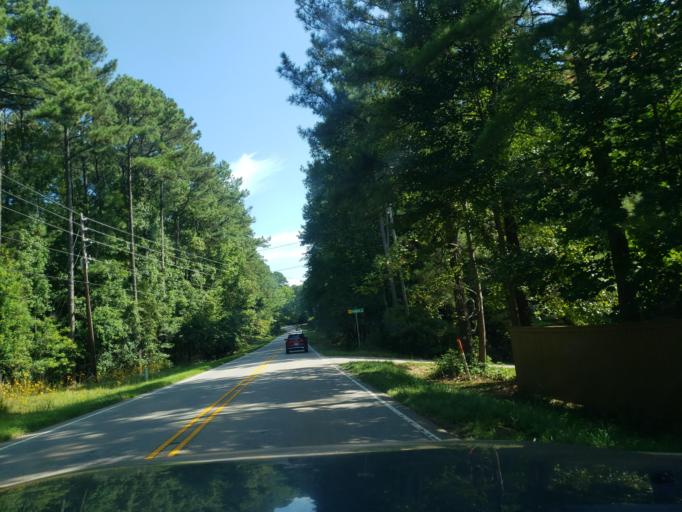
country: US
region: North Carolina
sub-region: Wake County
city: Morrisville
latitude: 35.9258
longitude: -78.7257
